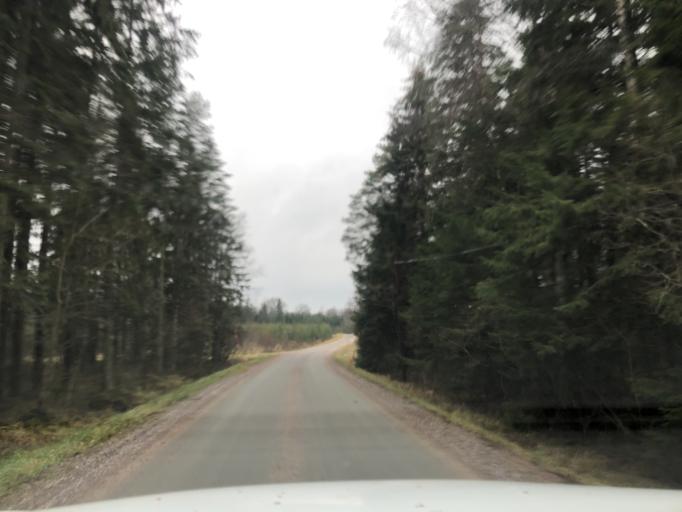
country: SE
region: Vaestra Goetaland
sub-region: Ulricehamns Kommun
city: Ulricehamn
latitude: 57.8614
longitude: 13.5992
